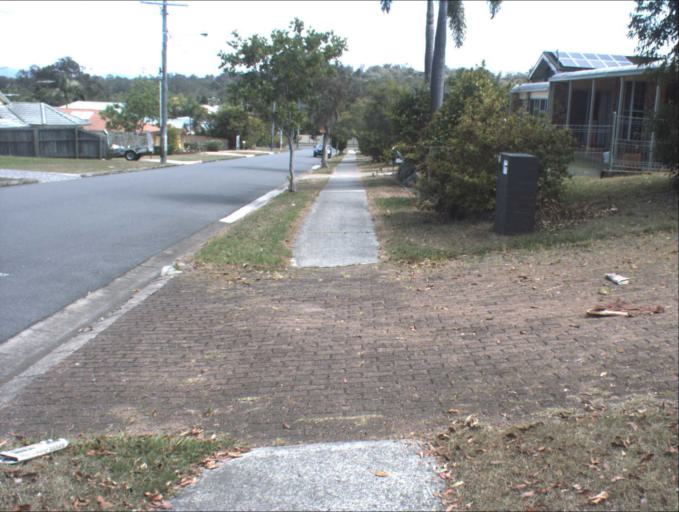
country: AU
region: Queensland
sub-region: Logan
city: Slacks Creek
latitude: -27.6595
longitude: 153.1761
